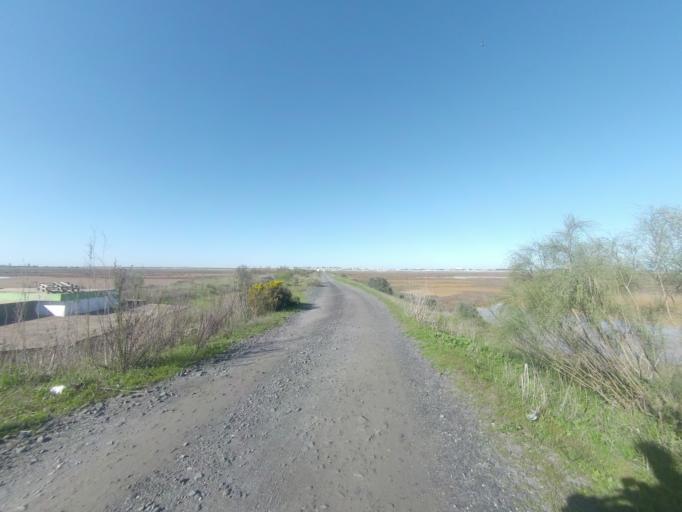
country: ES
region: Andalusia
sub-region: Provincia de Huelva
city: Palos de la Frontera
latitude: 37.2440
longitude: -6.8886
